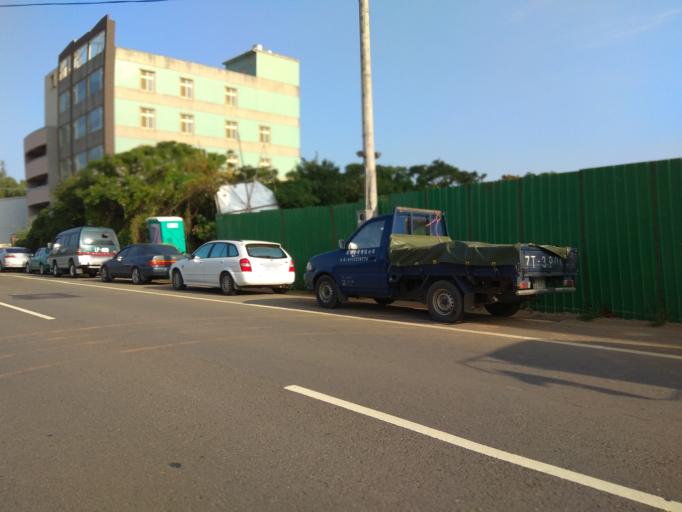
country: TW
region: Taiwan
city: Taoyuan City
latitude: 24.9652
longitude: 121.1419
